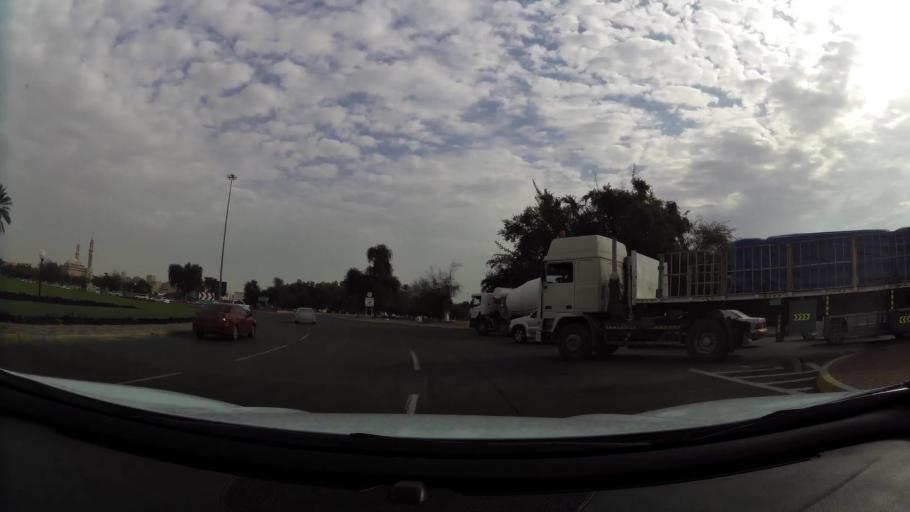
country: AE
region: Abu Dhabi
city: Al Ain
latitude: 24.1939
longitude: 55.6552
